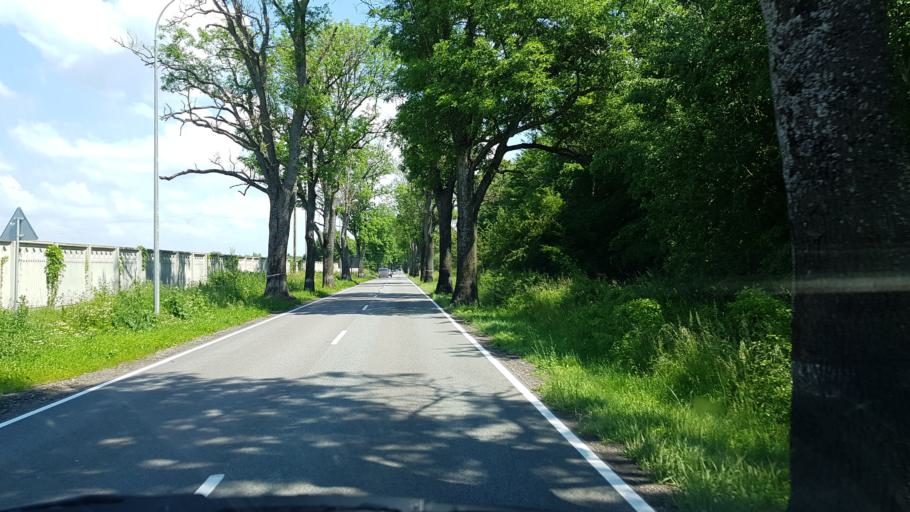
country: RU
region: Kaliningrad
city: Primorsk
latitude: 54.7398
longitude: 20.0505
